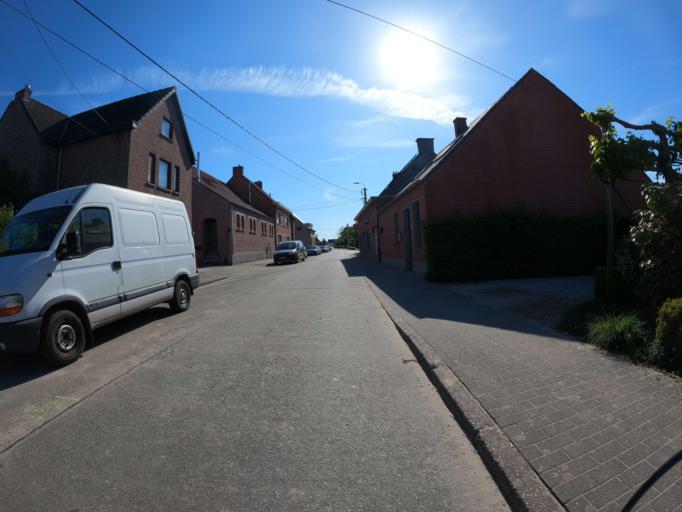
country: BE
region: Flanders
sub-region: Provincie Oost-Vlaanderen
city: Merelbeke
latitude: 50.9448
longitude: 3.7430
